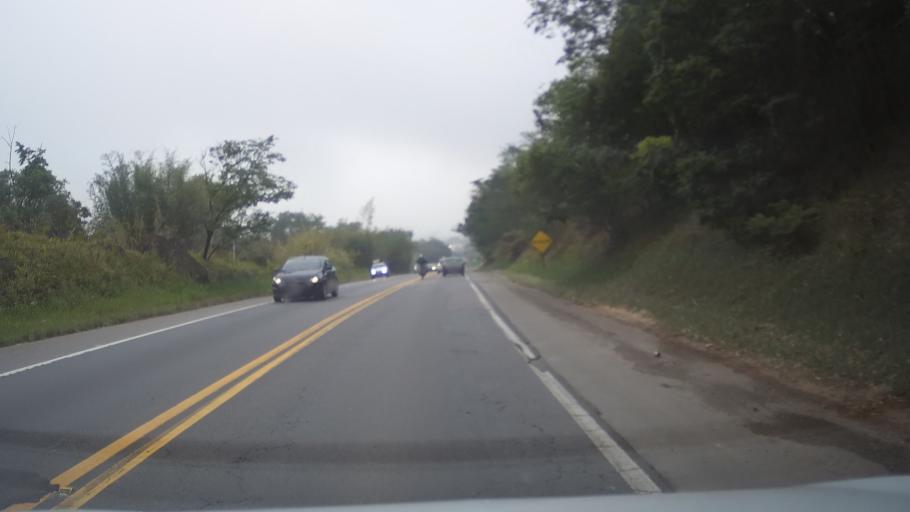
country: BR
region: Sao Paulo
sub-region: Itatiba
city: Itatiba
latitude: -22.9950
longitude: -46.8029
